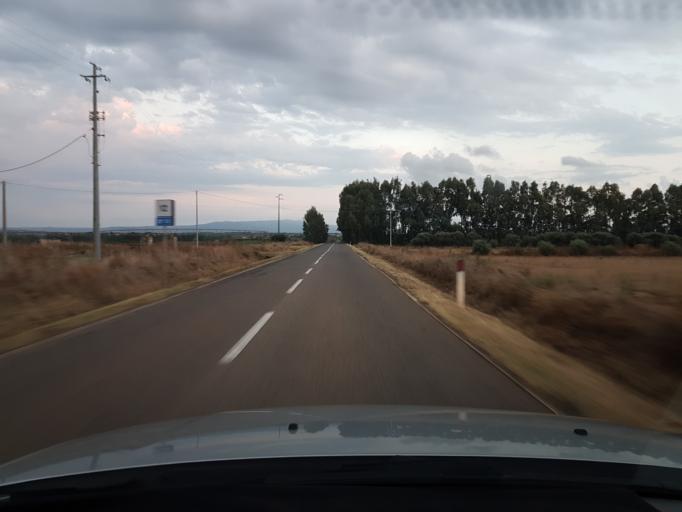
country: IT
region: Sardinia
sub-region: Provincia di Oristano
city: Tramatza
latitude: 40.0224
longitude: 8.6421
